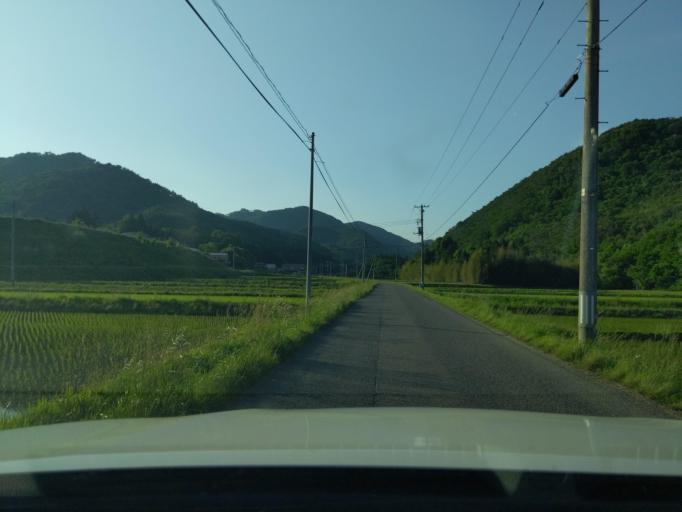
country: JP
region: Fukushima
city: Motomiya
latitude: 37.4939
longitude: 140.3281
